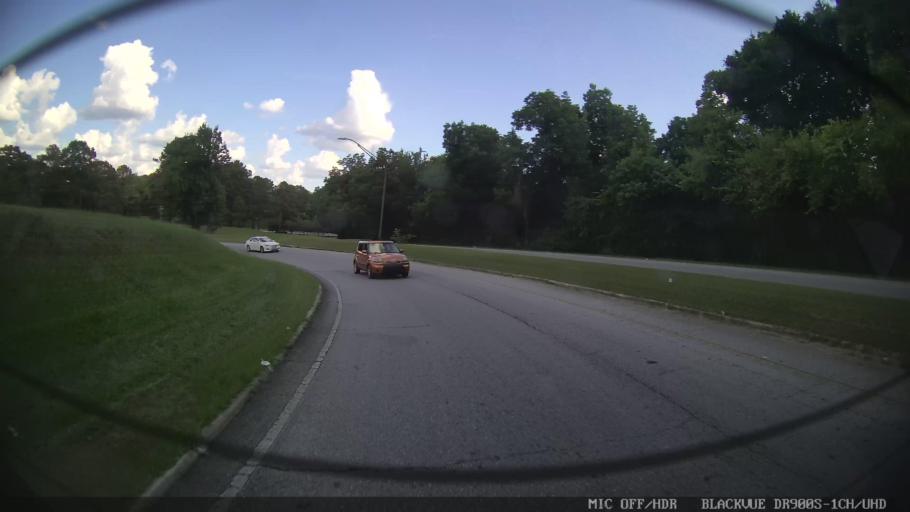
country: US
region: Georgia
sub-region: Floyd County
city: Rome
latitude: 34.2378
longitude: -85.1651
